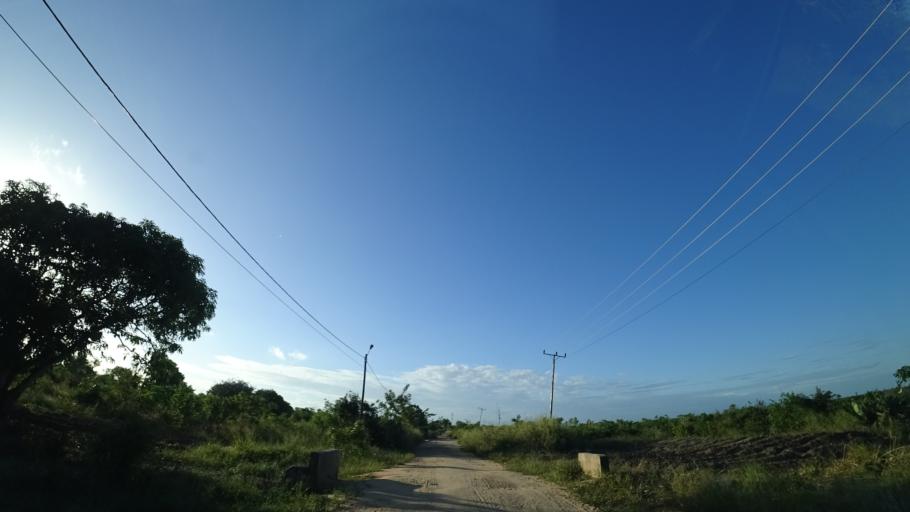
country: MZ
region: Sofala
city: Dondo
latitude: -19.3939
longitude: 34.7087
